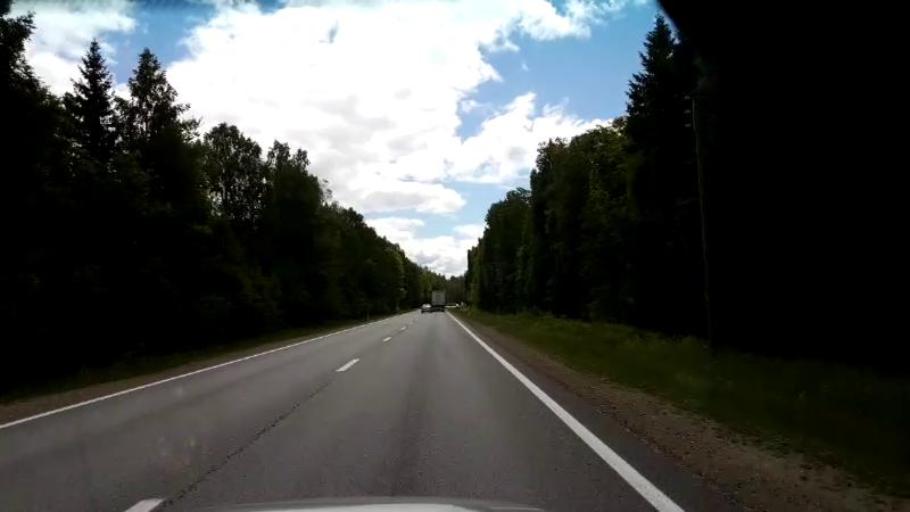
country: LV
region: Salacgrivas
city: Salacgriva
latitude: 57.5764
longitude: 24.4334
